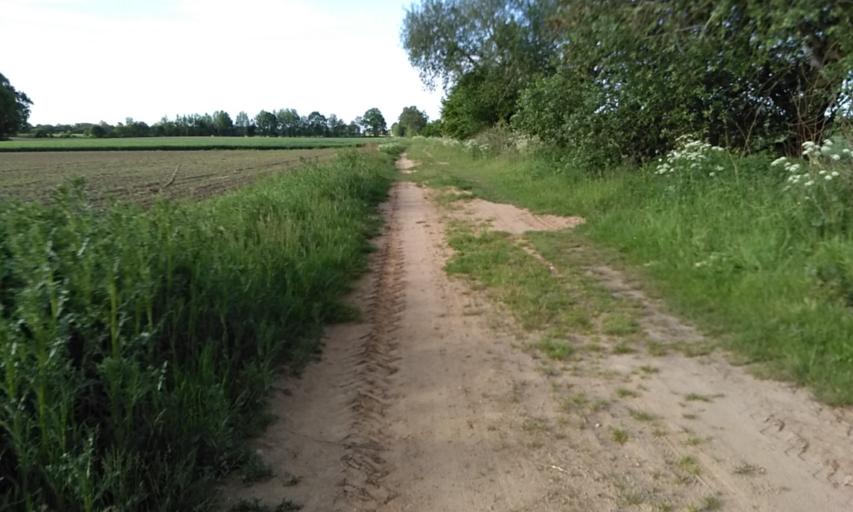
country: DE
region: Lower Saxony
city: Apensen
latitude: 53.4525
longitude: 9.6097
